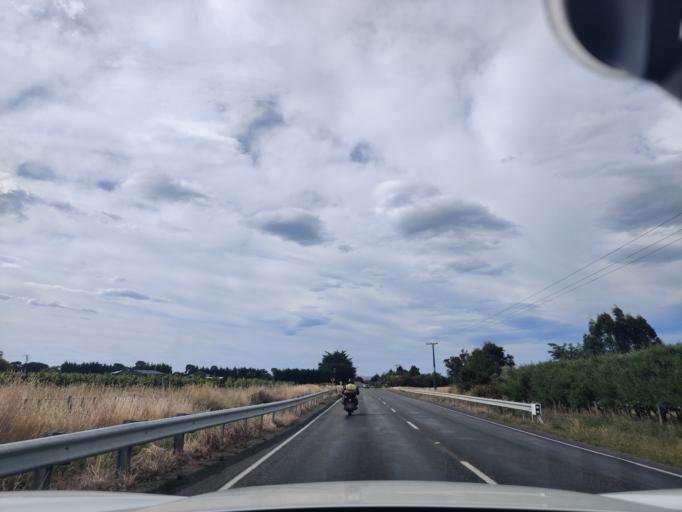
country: NZ
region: Wellington
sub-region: Masterton District
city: Masterton
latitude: -40.8888
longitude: 175.6601
